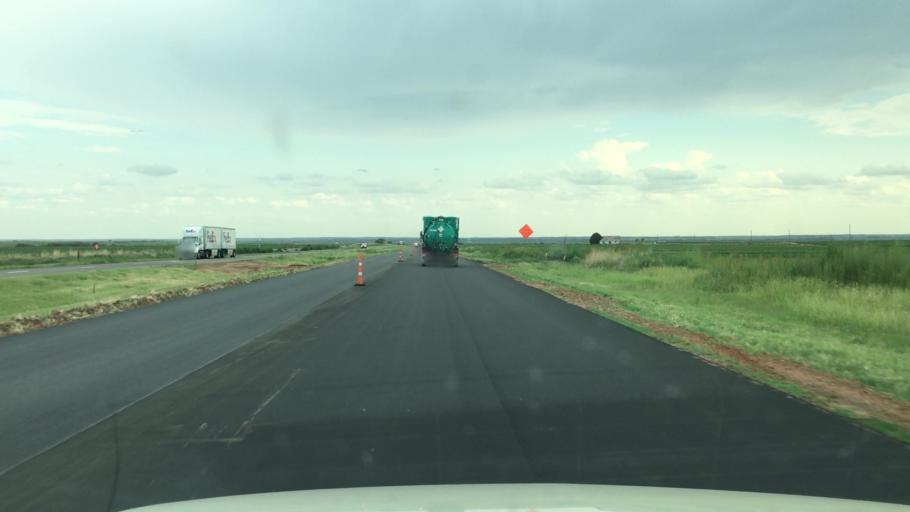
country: US
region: Texas
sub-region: Hall County
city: Memphis
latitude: 34.6200
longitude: -100.4721
